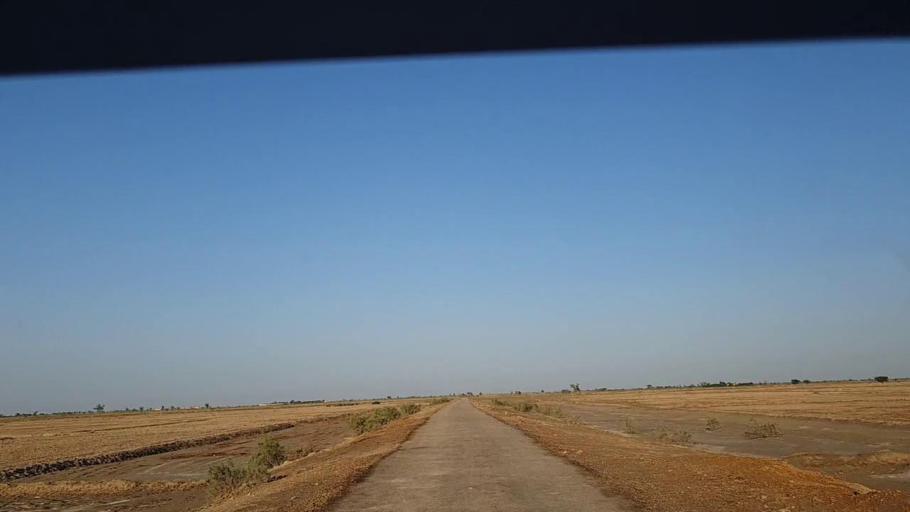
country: PK
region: Sindh
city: Johi
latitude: 26.7444
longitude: 67.6242
